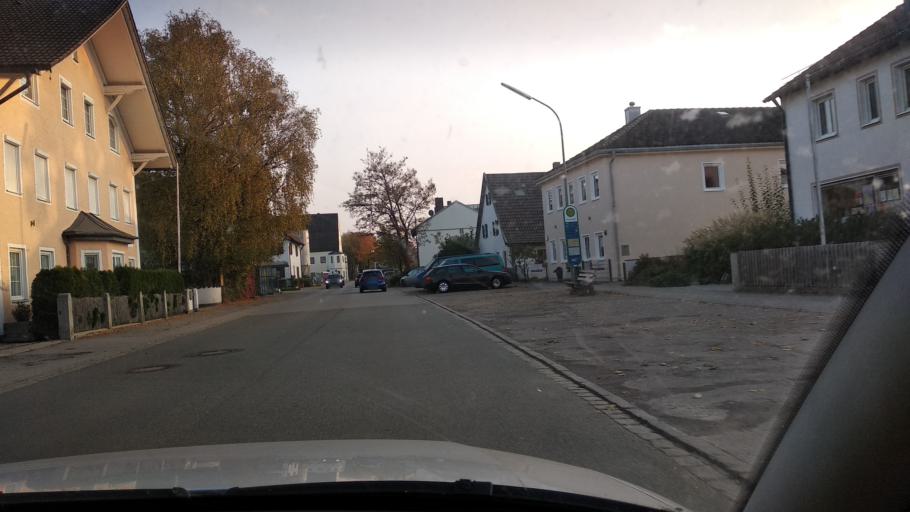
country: DE
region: Bavaria
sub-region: Upper Bavaria
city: Anzing
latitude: 48.1539
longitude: 11.8535
